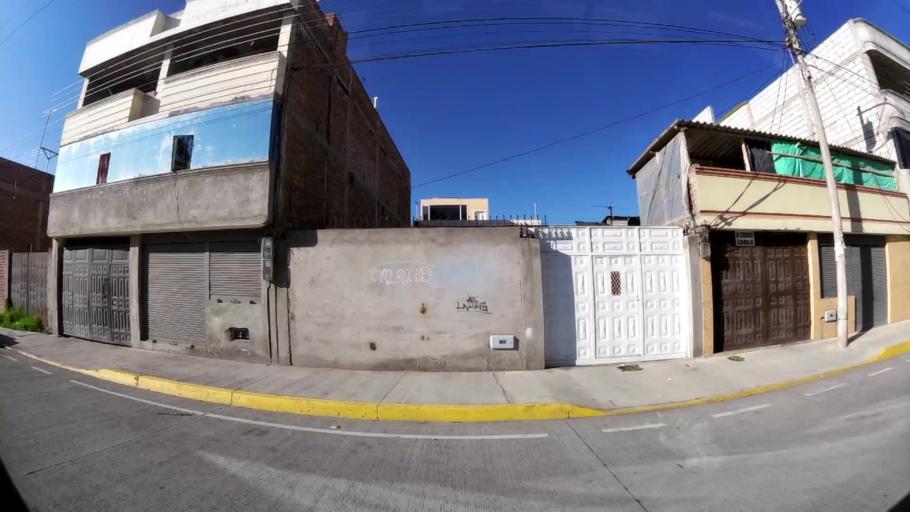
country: EC
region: Chimborazo
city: Riobamba
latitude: -1.6726
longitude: -78.6343
